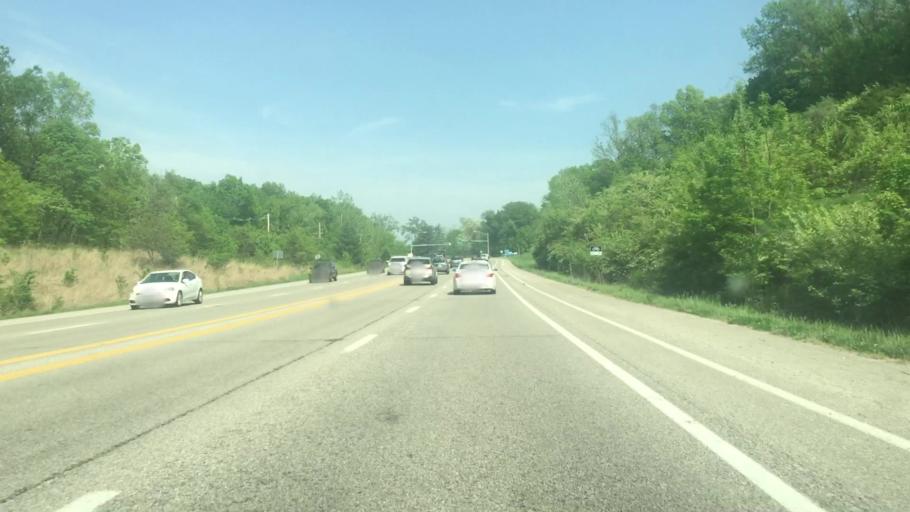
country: US
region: Missouri
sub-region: Boone County
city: Columbia
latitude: 38.9385
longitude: -92.3469
